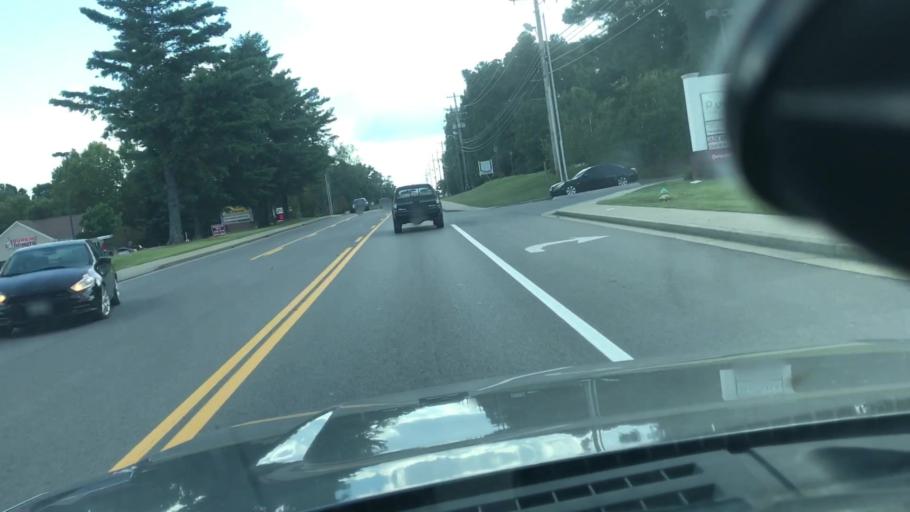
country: US
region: Tennessee
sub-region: Williamson County
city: Fairview
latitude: 35.9727
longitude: -87.1289
